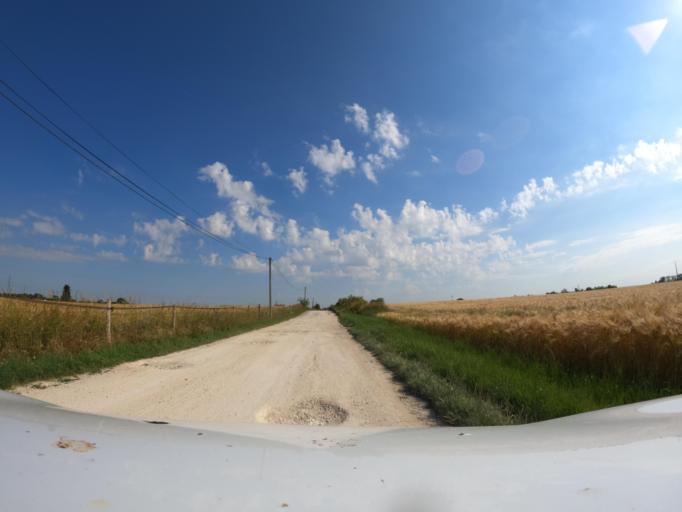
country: FR
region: Pays de la Loire
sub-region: Departement de la Vendee
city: Champagne-les-Marais
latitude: 46.3771
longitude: -1.1001
